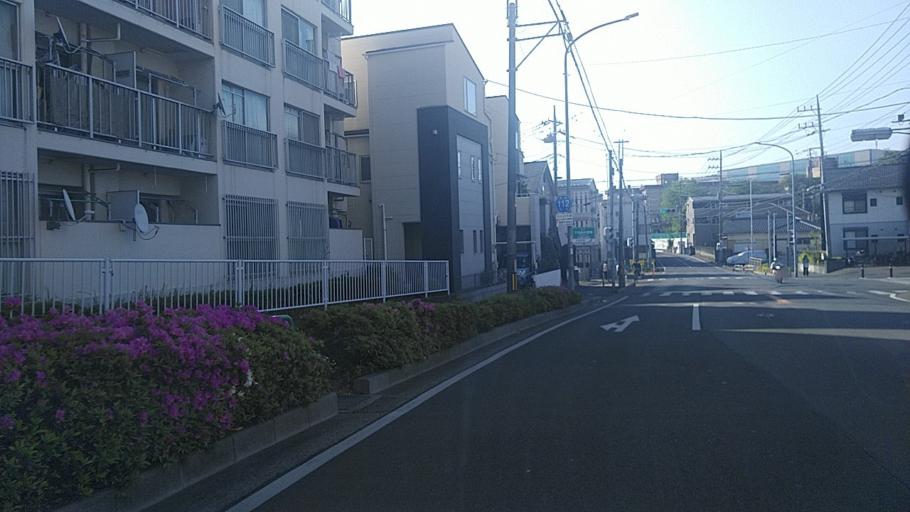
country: JP
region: Saitama
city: Asaka
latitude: 35.7941
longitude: 139.6051
